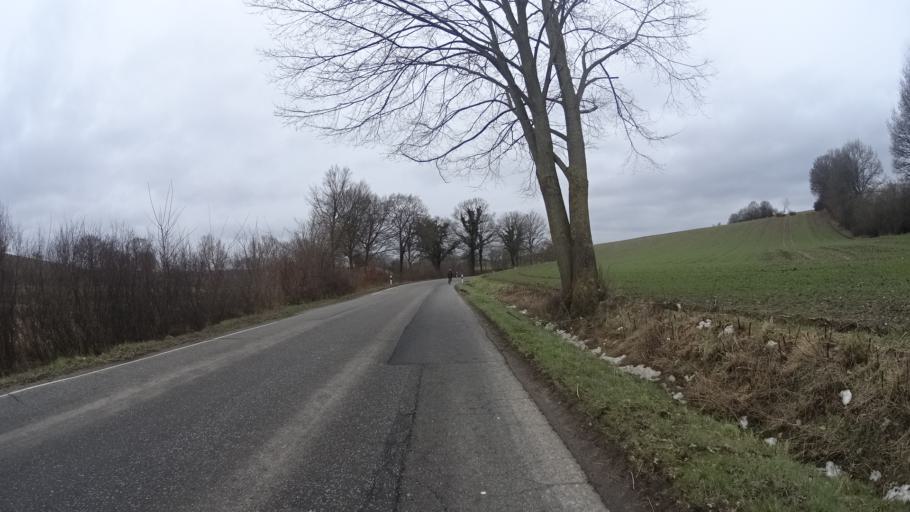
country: DE
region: Schleswig-Holstein
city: Neukirchen
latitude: 54.2099
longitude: 10.5564
